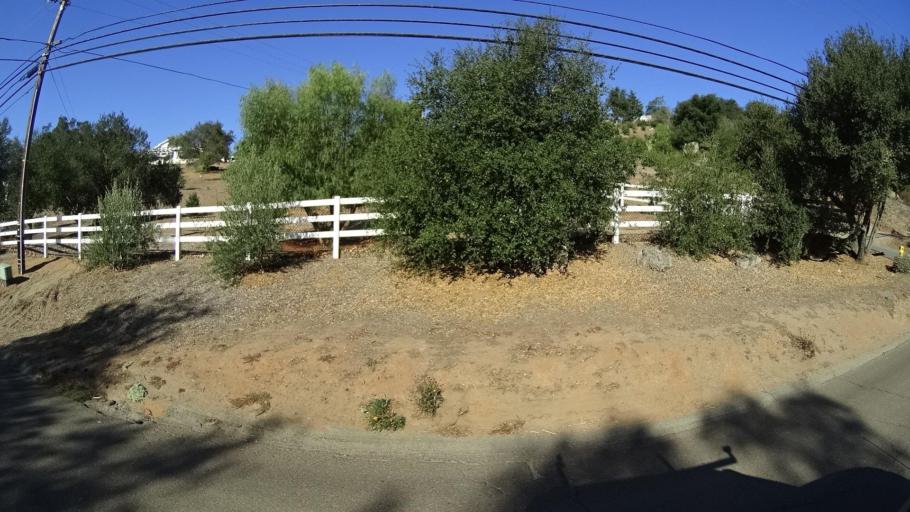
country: US
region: California
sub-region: San Diego County
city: Hidden Meadows
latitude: 33.2213
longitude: -117.1107
